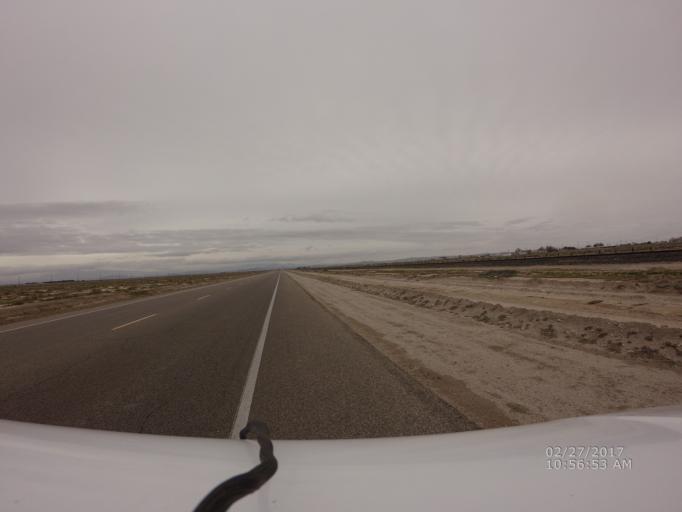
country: US
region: California
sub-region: Los Angeles County
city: Lancaster
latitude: 34.7415
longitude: -118.1435
